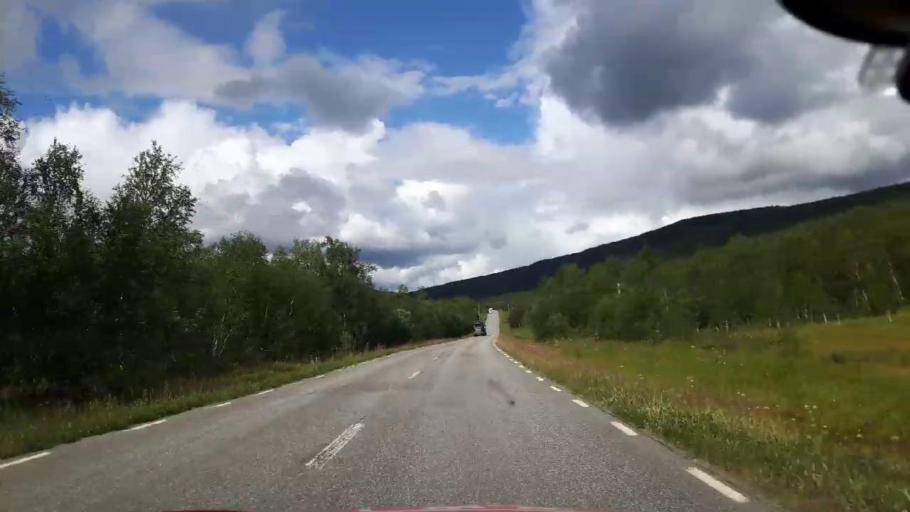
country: NO
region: Nordland
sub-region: Hattfjelldal
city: Hattfjelldal
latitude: 65.0549
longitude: 14.7294
